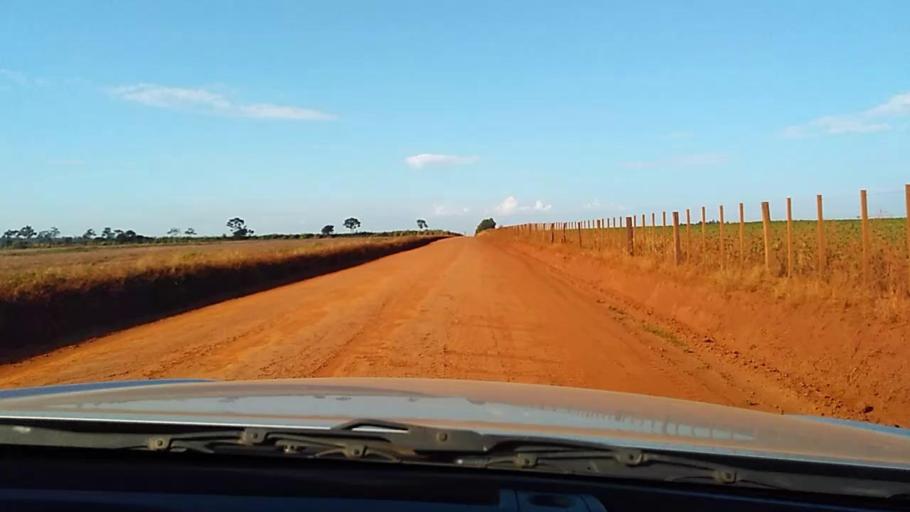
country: PY
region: Alto Parana
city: Naranjal
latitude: -25.7120
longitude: -55.3911
